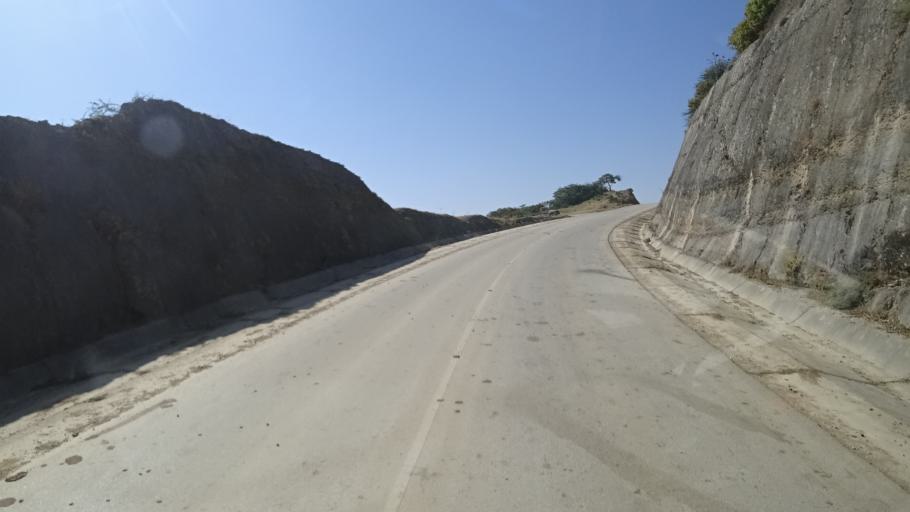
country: OM
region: Zufar
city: Salalah
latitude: 17.0612
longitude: 54.6064
